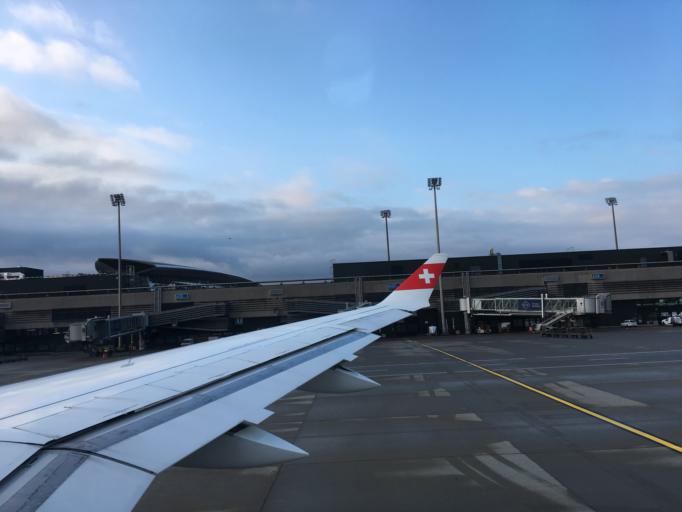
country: CH
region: Zurich
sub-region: Bezirk Buelach
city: Kloten / Holberg
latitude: 47.4549
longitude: 8.5601
